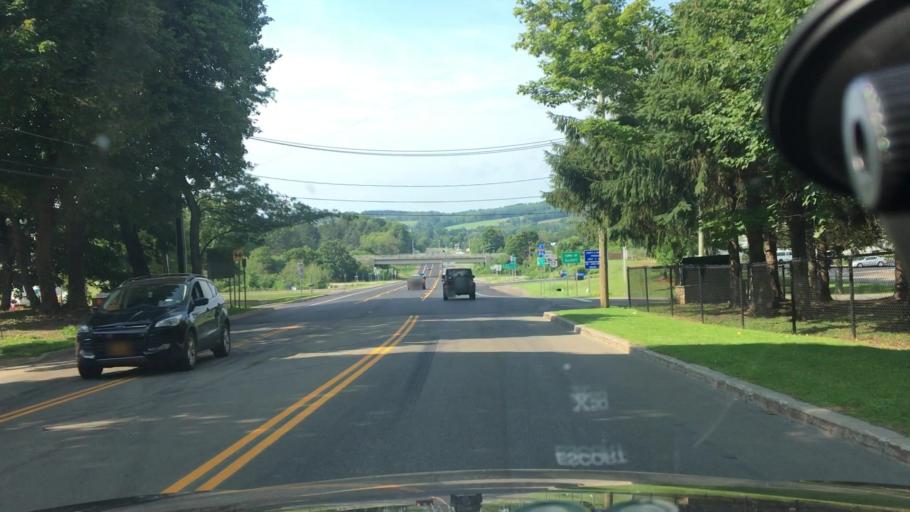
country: US
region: New York
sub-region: Chautauqua County
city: Jamestown
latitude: 42.1185
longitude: -79.2408
